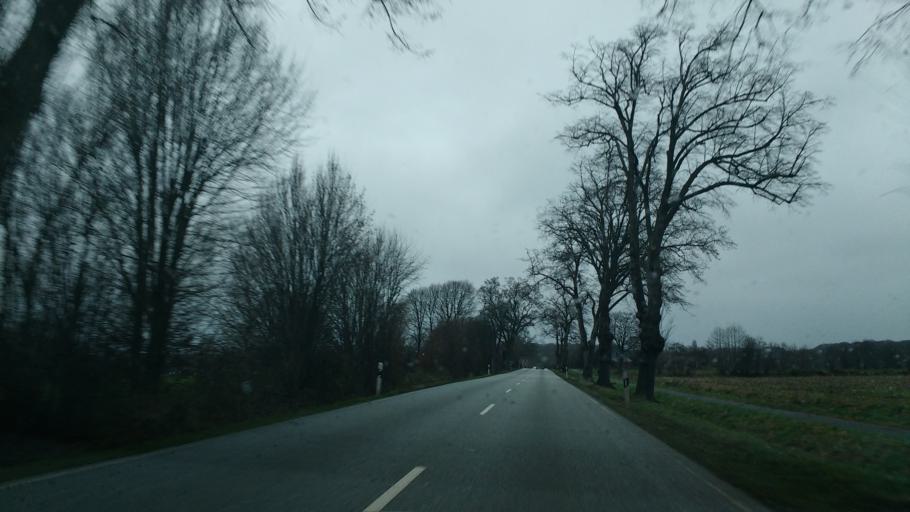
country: DE
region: Schleswig-Holstein
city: Jahrsdorf
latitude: 54.0613
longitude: 9.6355
